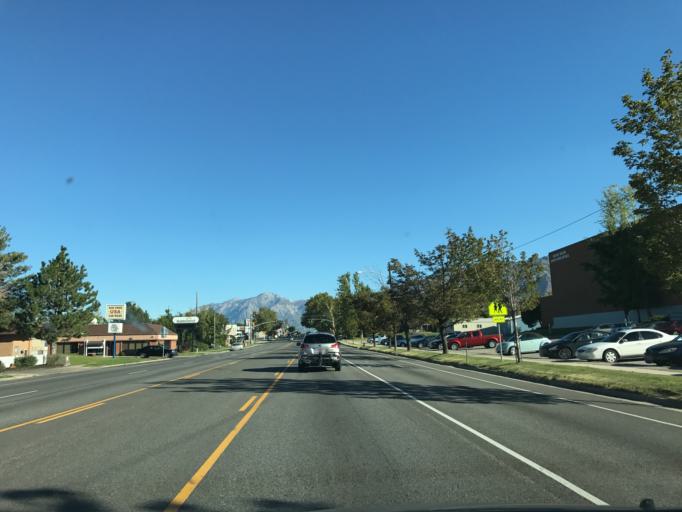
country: US
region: Utah
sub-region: Weber County
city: South Ogden
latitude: 41.2041
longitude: -111.9486
